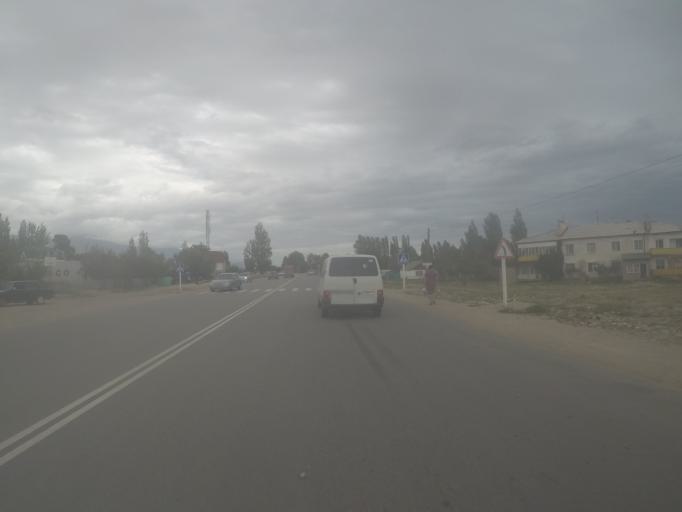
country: KG
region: Ysyk-Koel
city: Cholpon-Ata
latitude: 42.5853
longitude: 76.7394
